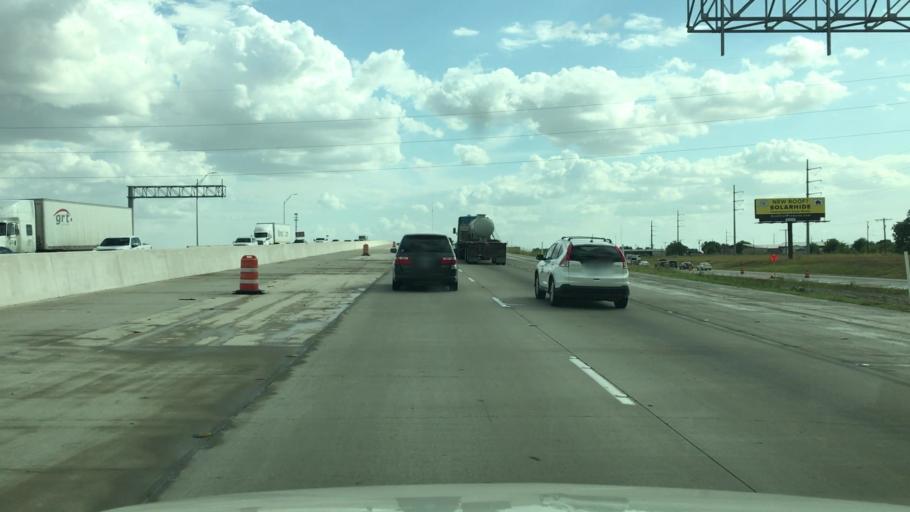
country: US
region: Texas
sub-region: McLennan County
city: Bruceville-Eddy
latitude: 31.3109
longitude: -97.2427
